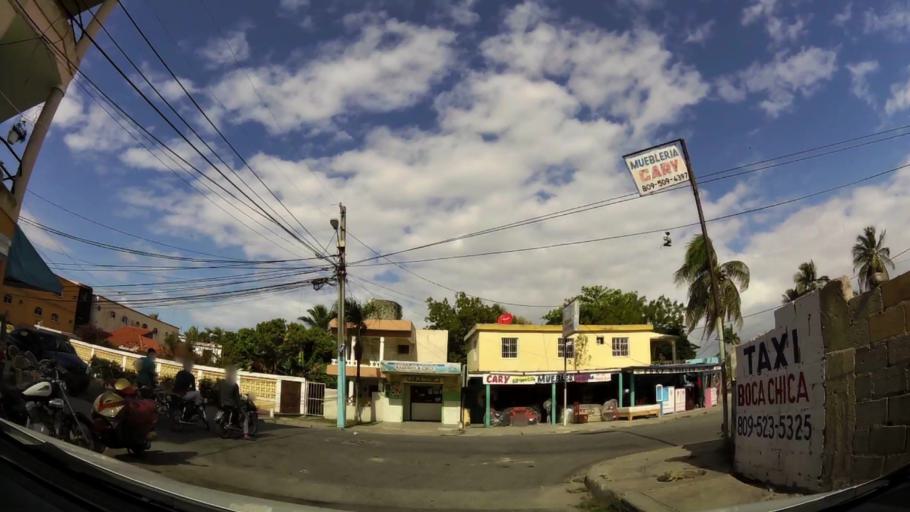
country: DO
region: Santo Domingo
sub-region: Santo Domingo
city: Boca Chica
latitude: 18.4544
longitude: -69.6082
